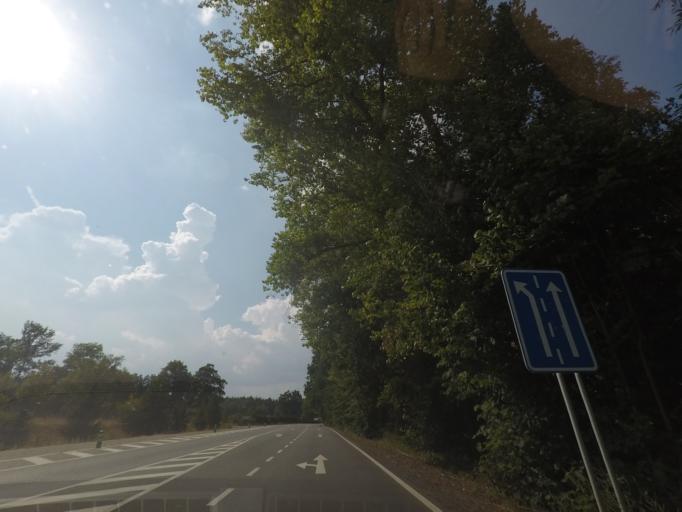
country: CZ
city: Borohradek
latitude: 50.1034
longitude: 16.0849
